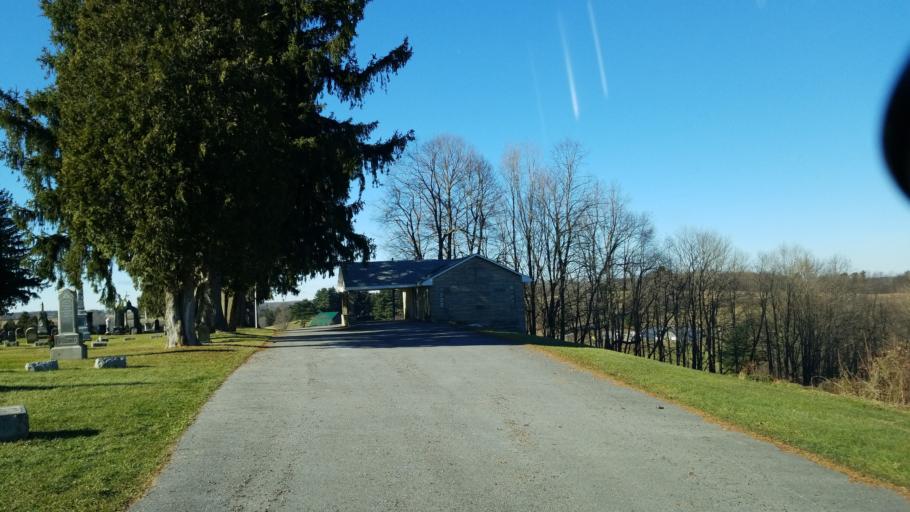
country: US
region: Pennsylvania
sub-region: Jefferson County
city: Falls Creek
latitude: 41.1807
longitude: -78.8626
